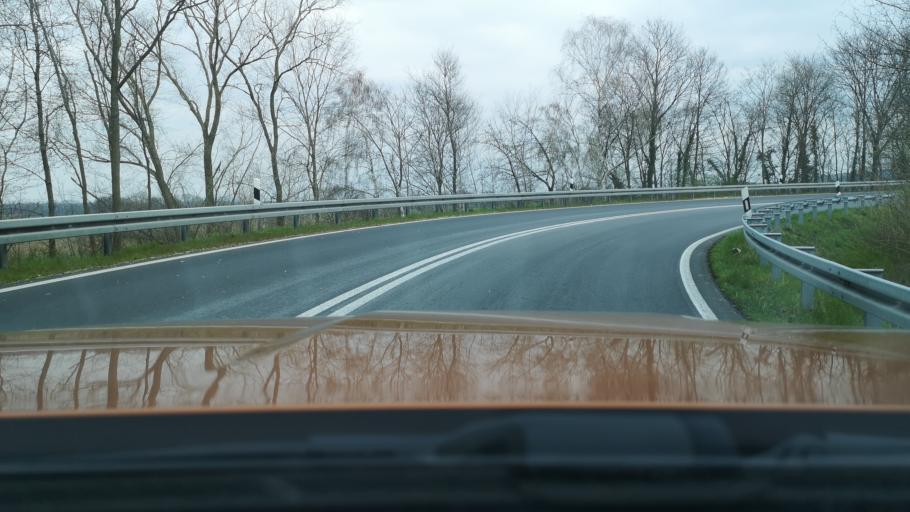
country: DE
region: Lower Saxony
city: Lauenhagen
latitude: 52.3316
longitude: 9.2356
